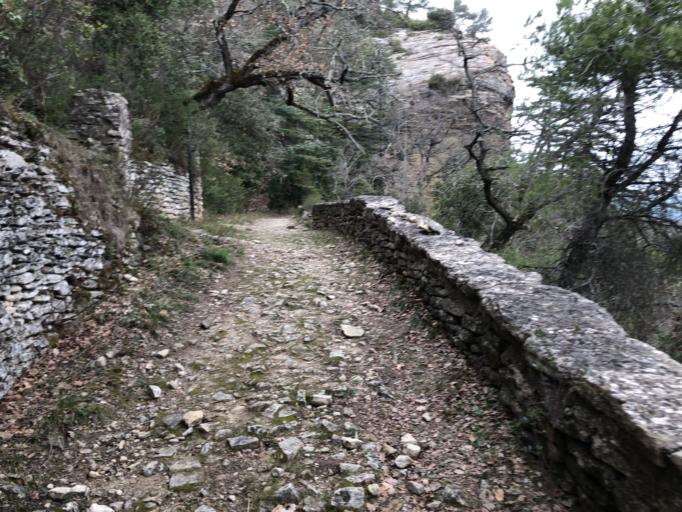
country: FR
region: Provence-Alpes-Cote d'Azur
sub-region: Departement du Vaucluse
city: Goult
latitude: 43.8612
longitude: 5.2307
